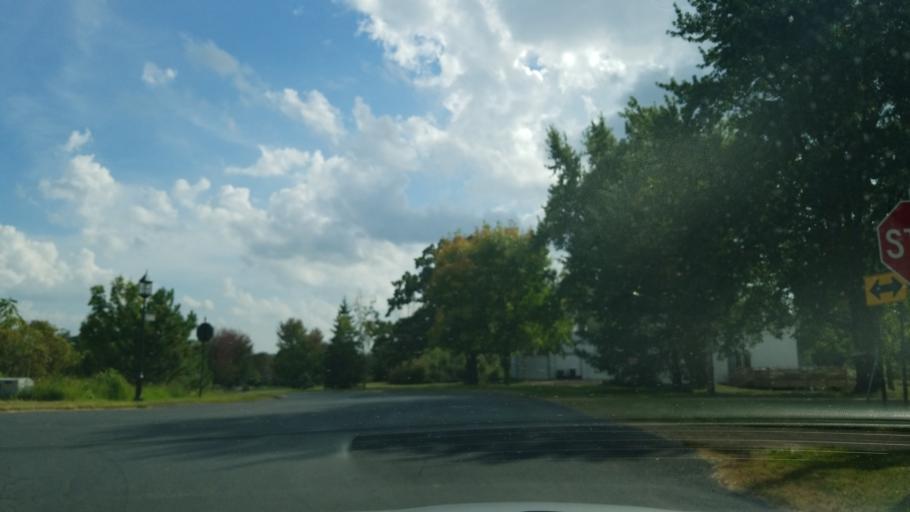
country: US
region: Minnesota
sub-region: Washington County
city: Lake Saint Croix Beach
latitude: 44.9058
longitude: -92.7363
